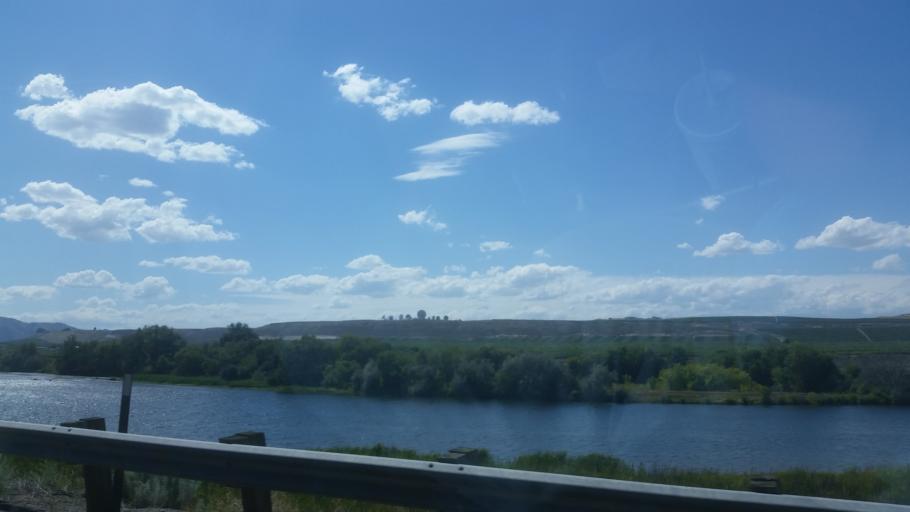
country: US
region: Washington
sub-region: Okanogan County
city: Brewster
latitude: 48.1558
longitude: -119.6633
